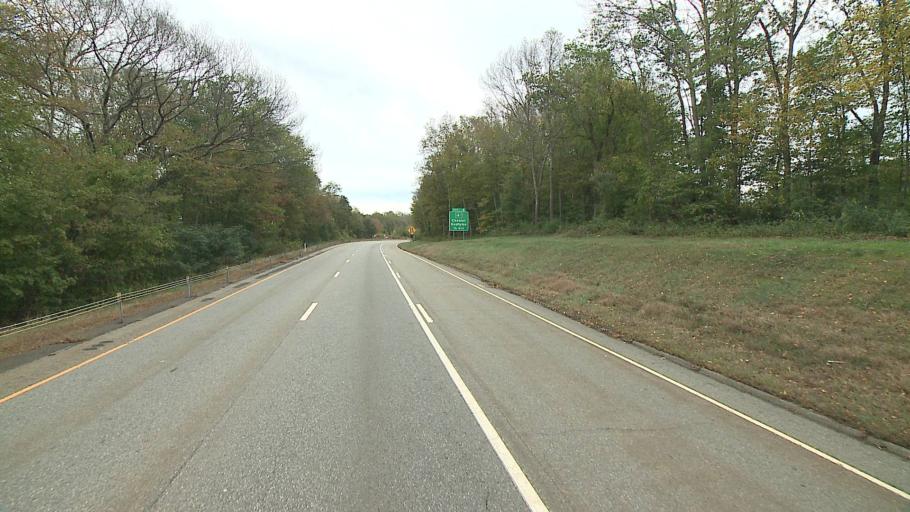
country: US
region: Connecticut
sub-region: Middlesex County
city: Chester Center
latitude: 41.4098
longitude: -72.4800
